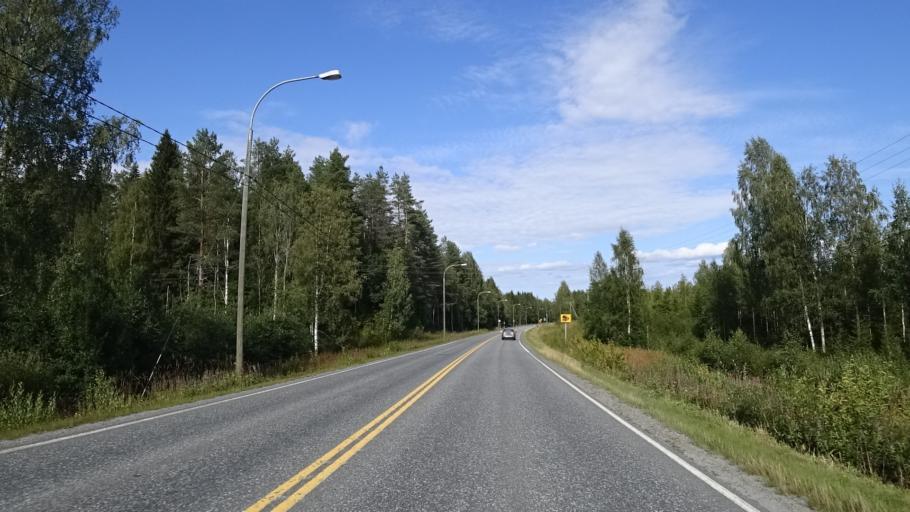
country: FI
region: North Karelia
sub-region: Joensuu
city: Eno
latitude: 62.7925
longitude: 30.0863
